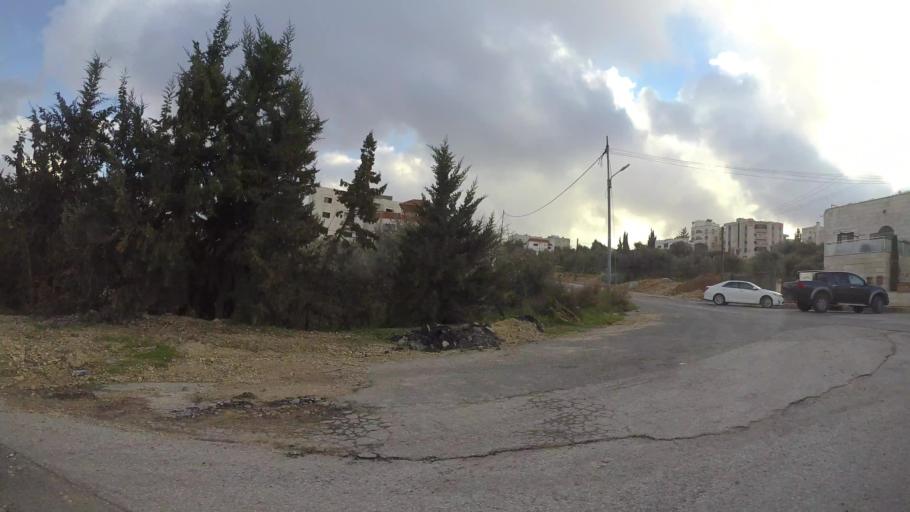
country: JO
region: Amman
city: Al Jubayhah
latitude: 32.0541
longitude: 35.8901
